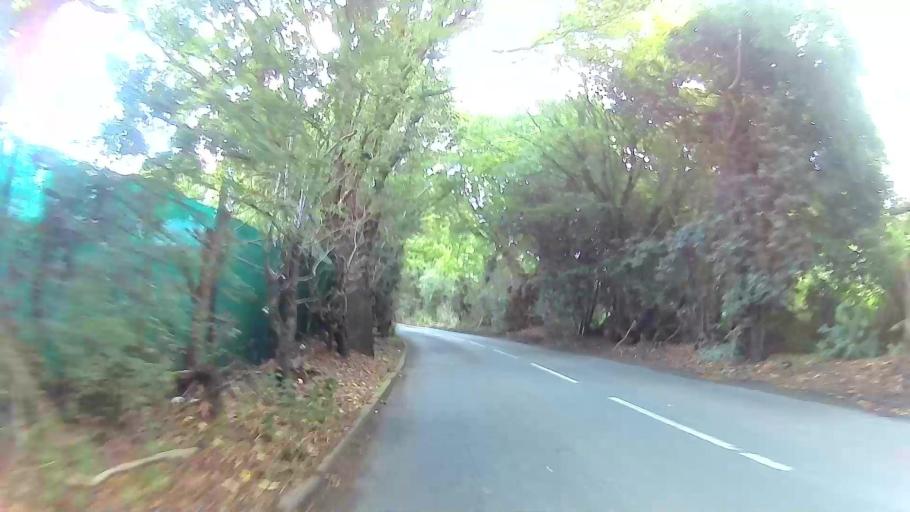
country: GB
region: England
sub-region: Greater London
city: Hainault
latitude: 51.6327
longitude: 0.1387
